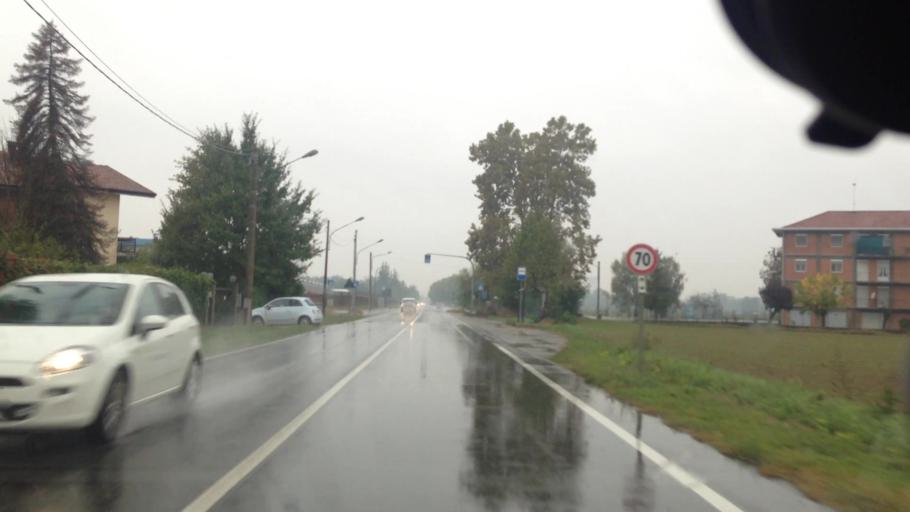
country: IT
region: Piedmont
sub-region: Provincia di Alessandria
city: Felizzano
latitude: 44.9001
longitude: 8.4255
